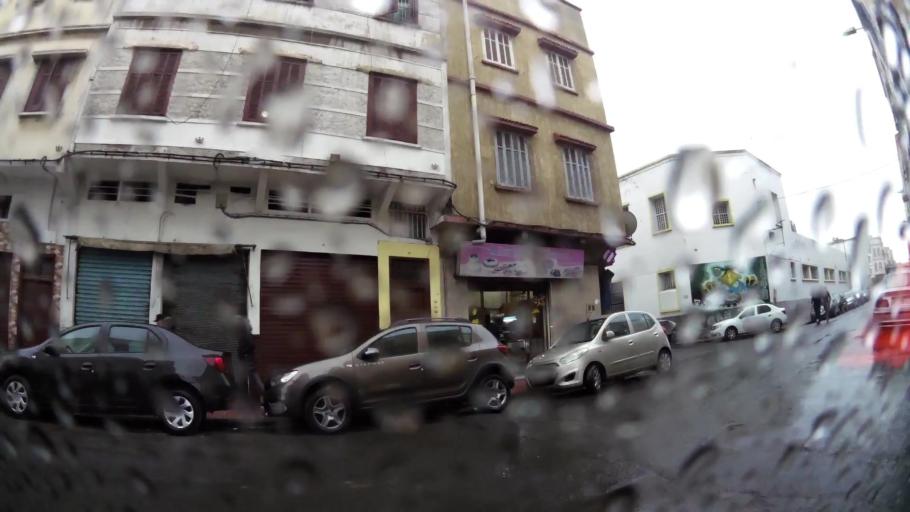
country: MA
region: Grand Casablanca
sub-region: Casablanca
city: Casablanca
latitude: 33.5708
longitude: -7.6055
